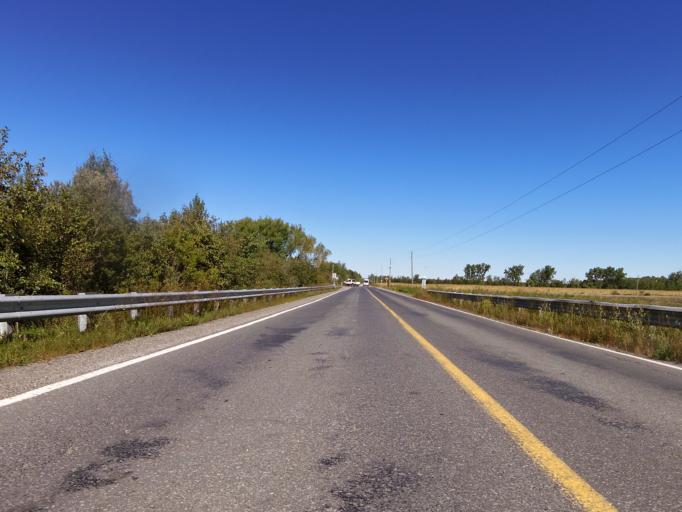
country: CA
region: Ontario
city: Clarence-Rockland
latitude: 45.3313
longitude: -75.4170
